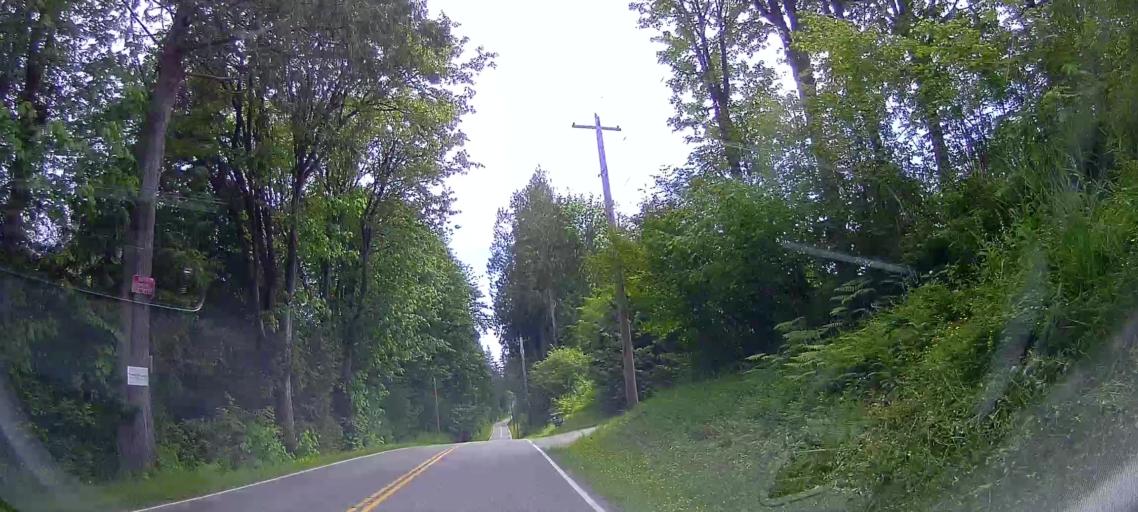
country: US
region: Washington
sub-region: Snohomish County
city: Bryant
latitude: 48.2391
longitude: -122.1998
